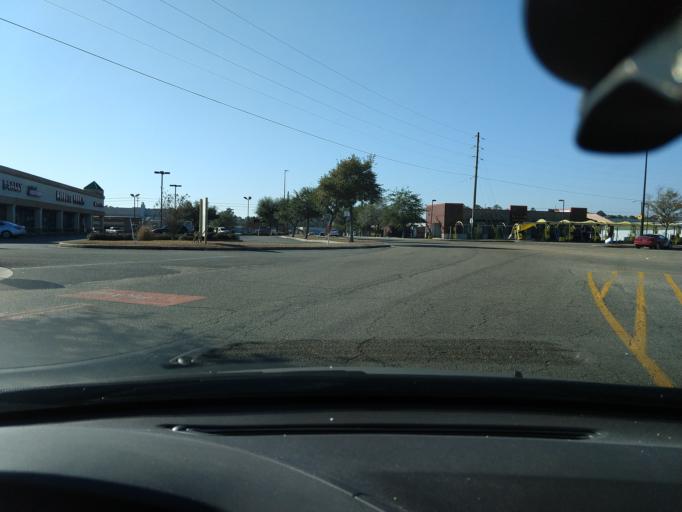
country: US
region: Mississippi
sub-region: Jackson County
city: Gulf Park Estates
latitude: 30.4107
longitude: -88.7593
